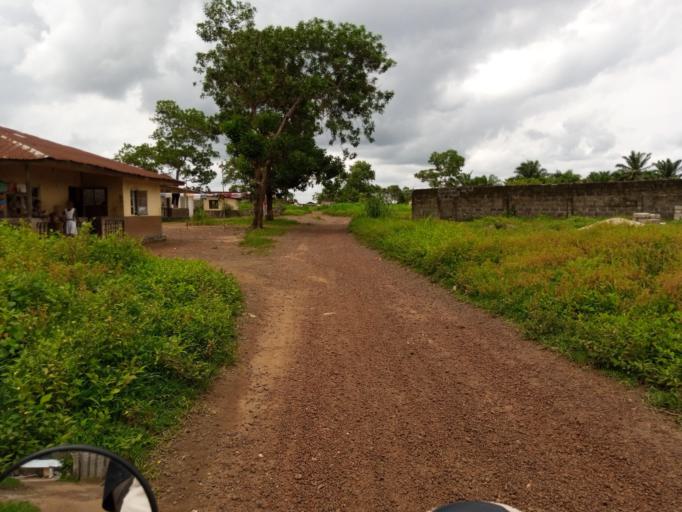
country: SL
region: Southern Province
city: Moyamba
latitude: 8.1641
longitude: -12.4246
